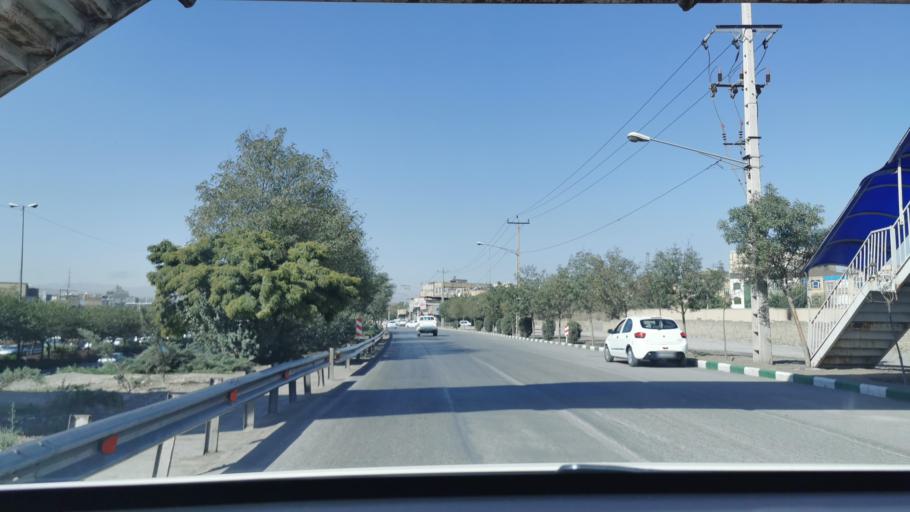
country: IR
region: Razavi Khorasan
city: Mashhad
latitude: 36.3501
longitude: 59.5713
